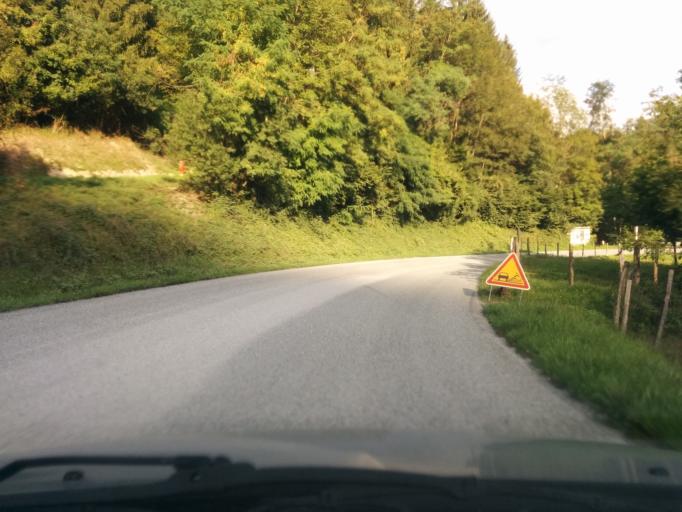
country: FR
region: Rhone-Alpes
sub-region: Departement de la Savoie
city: Saint-Beron
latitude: 45.4729
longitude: 5.7381
